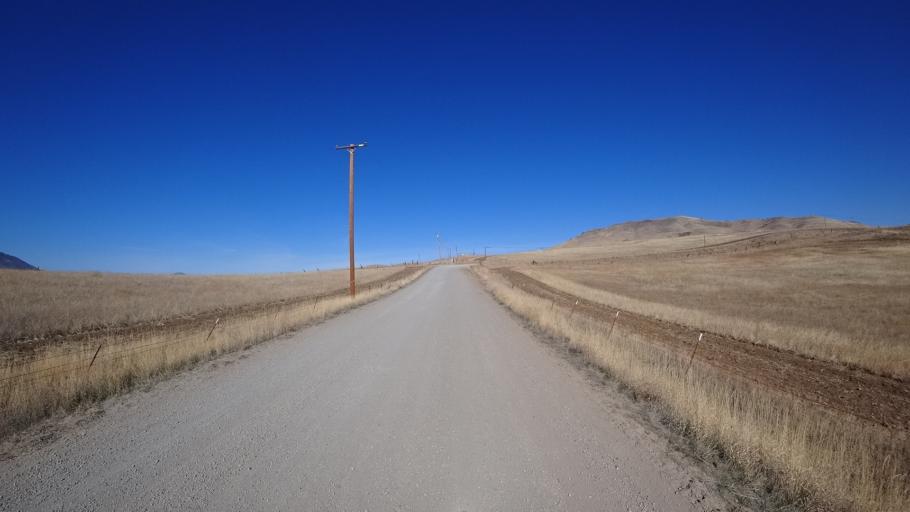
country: US
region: California
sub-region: Siskiyou County
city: Montague
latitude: 41.8288
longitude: -122.4205
